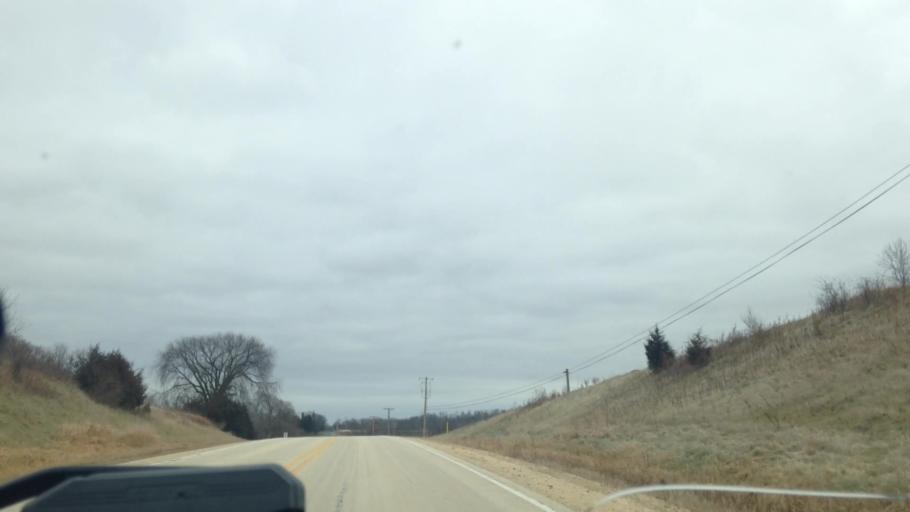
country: US
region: Wisconsin
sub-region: Dodge County
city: Mayville
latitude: 43.4935
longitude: -88.5273
